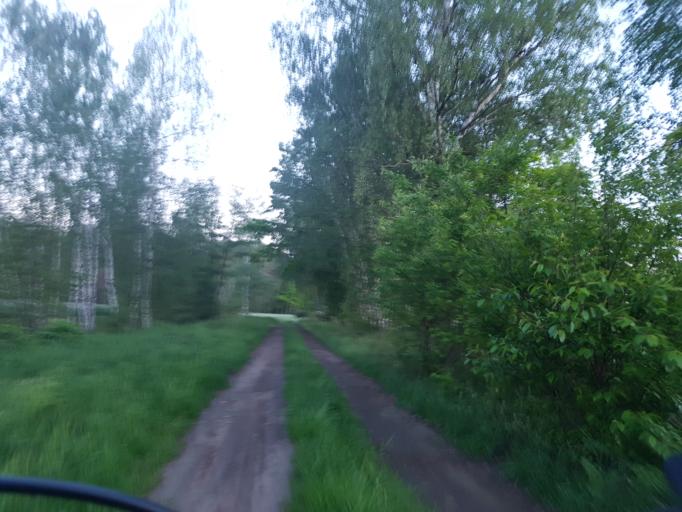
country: DE
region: Brandenburg
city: Schilda
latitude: 51.5666
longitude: 13.3740
